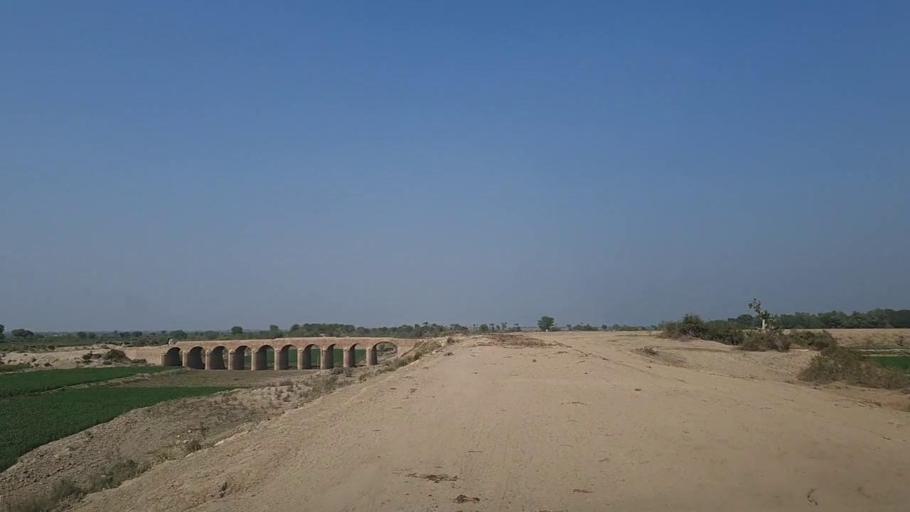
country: PK
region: Sindh
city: Naushahro Firoz
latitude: 26.8534
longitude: 67.9585
